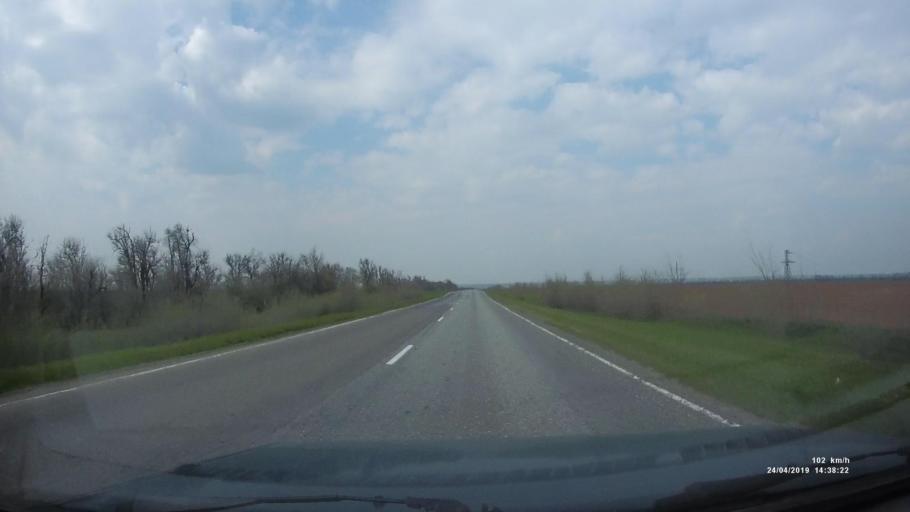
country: RU
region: Rostov
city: Remontnoye
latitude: 46.4002
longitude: 43.8861
